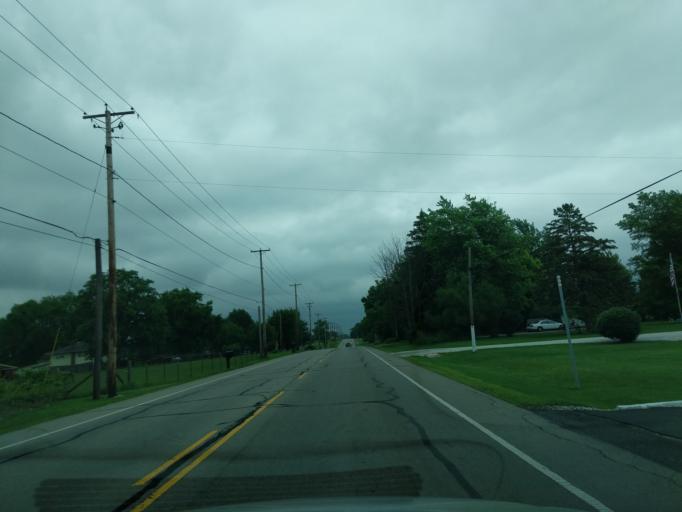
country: US
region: Indiana
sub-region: Madison County
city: Alexandria
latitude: 40.2779
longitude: -85.6637
